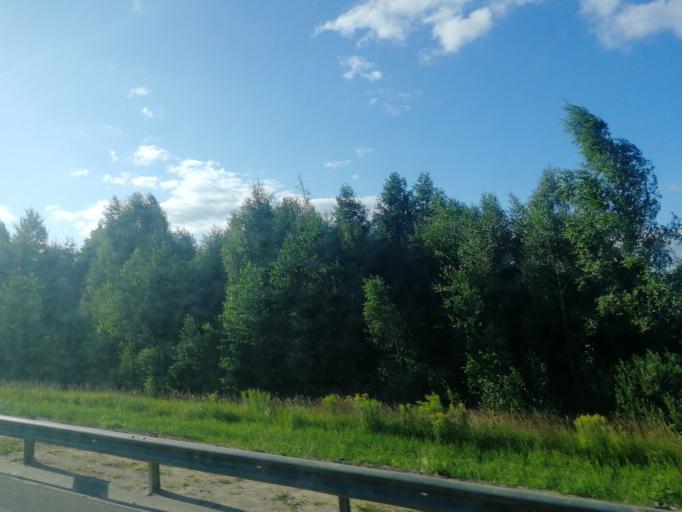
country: RU
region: Tula
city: Novogurovskiy
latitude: 54.2808
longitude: 37.1867
